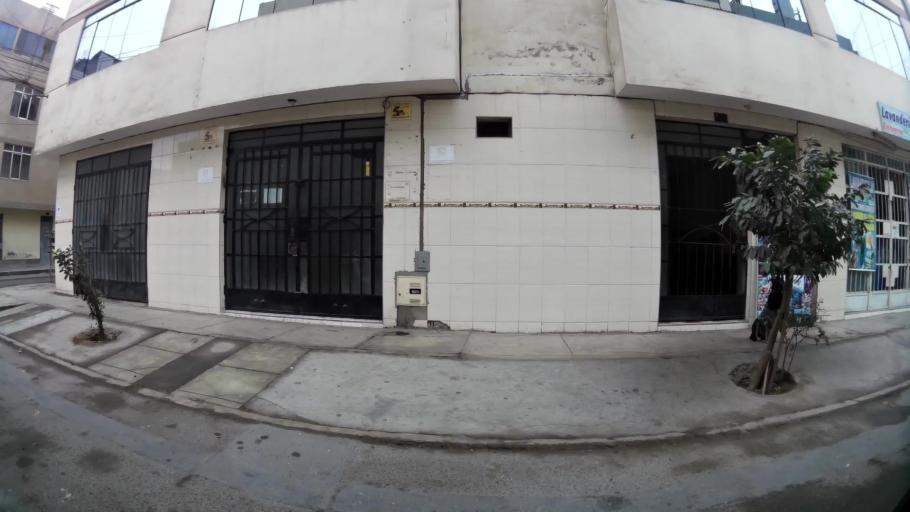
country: PE
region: Lima
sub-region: Lima
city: Independencia
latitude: -11.9740
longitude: -77.0729
